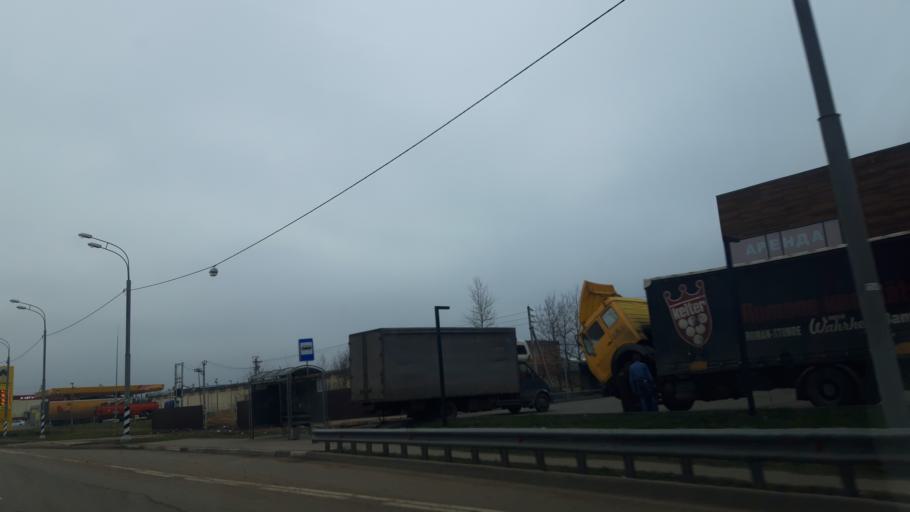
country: RU
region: Moskovskaya
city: Lozhki
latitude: 56.0990
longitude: 37.1030
